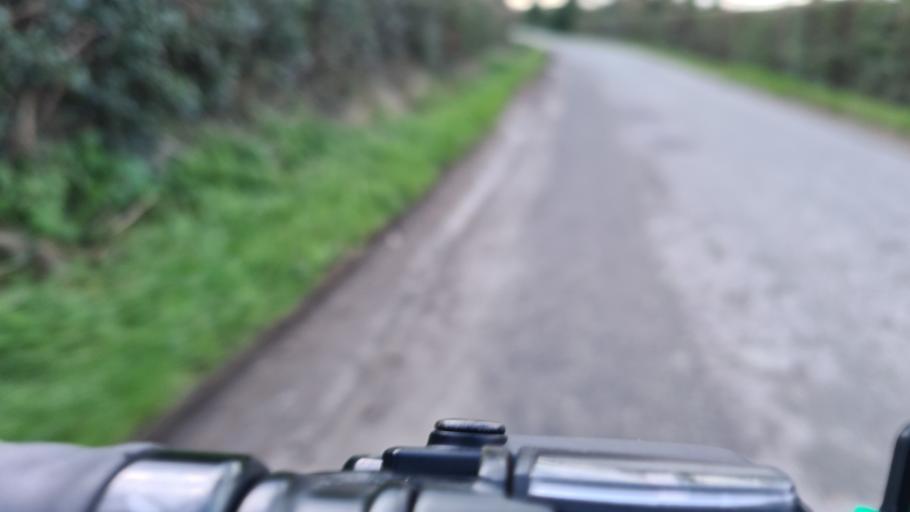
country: IE
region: Leinster
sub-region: Kildare
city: Celbridge
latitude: 53.3494
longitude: -6.5775
